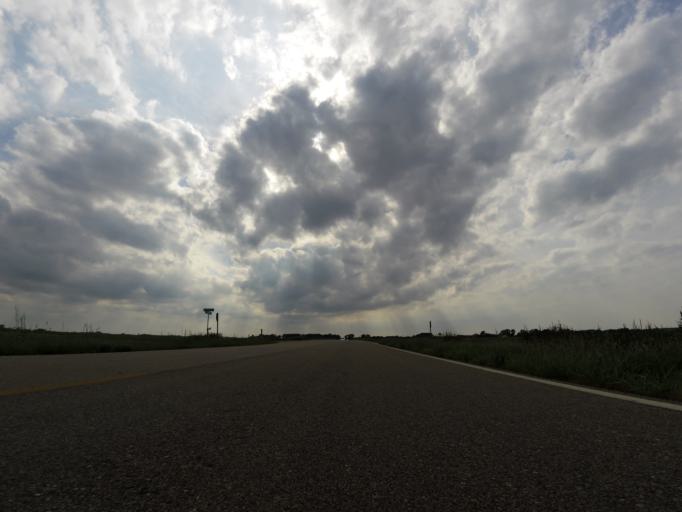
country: US
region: Kansas
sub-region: Reno County
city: South Hutchinson
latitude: 37.8977
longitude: -98.0500
